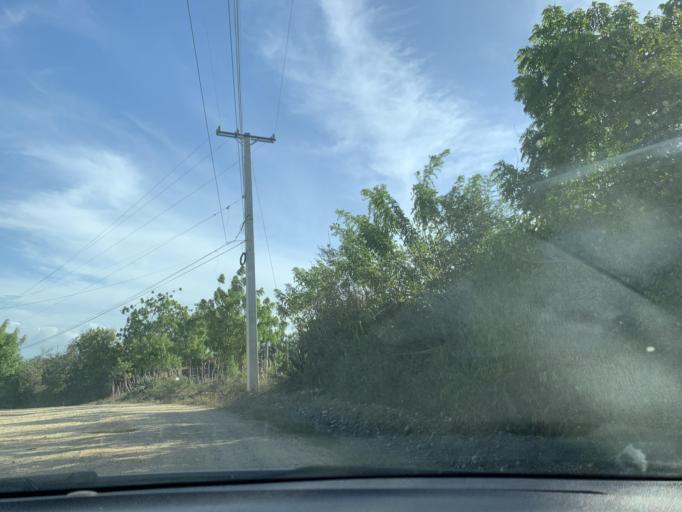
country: DO
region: Puerto Plata
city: Luperon
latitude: 19.8732
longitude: -70.9399
